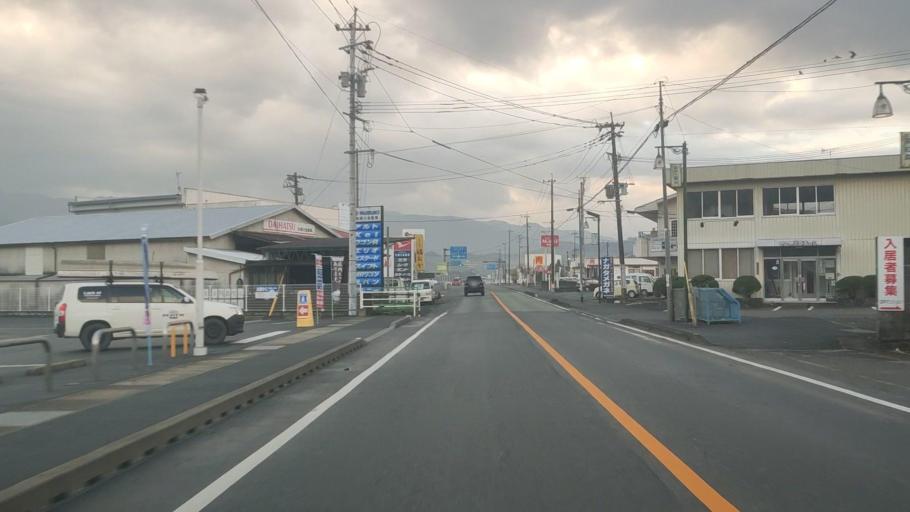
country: JP
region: Kumamoto
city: Matsubase
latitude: 32.6499
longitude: 130.8111
